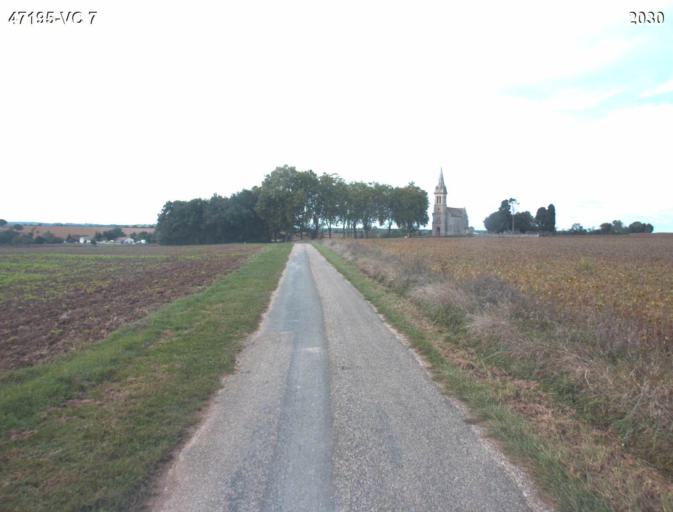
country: FR
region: Aquitaine
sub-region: Departement du Lot-et-Garonne
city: Nerac
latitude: 44.1000
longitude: 0.3380
